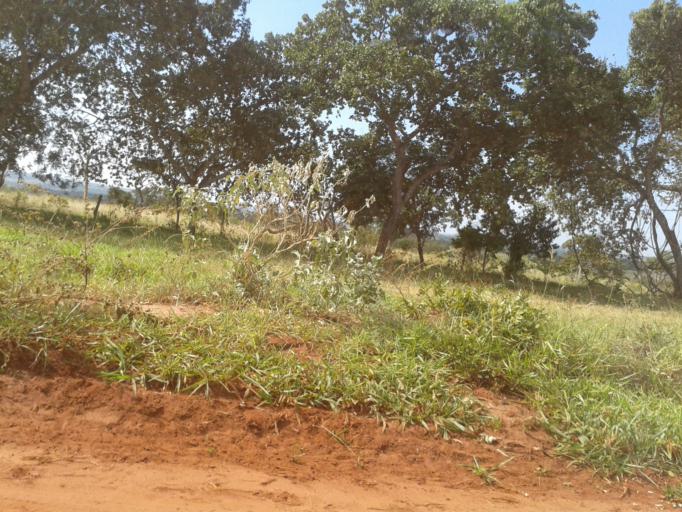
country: BR
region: Minas Gerais
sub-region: Ituiutaba
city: Ituiutaba
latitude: -19.0629
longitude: -49.3643
